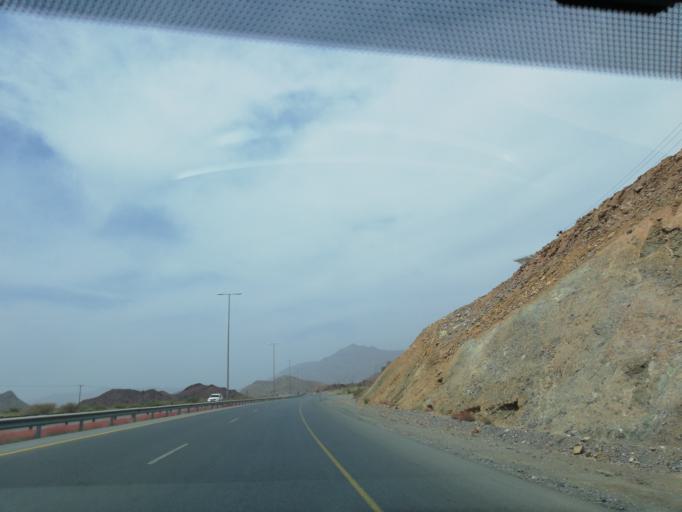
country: OM
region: Muhafazat ad Dakhiliyah
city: Izki
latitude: 22.8828
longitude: 57.7032
